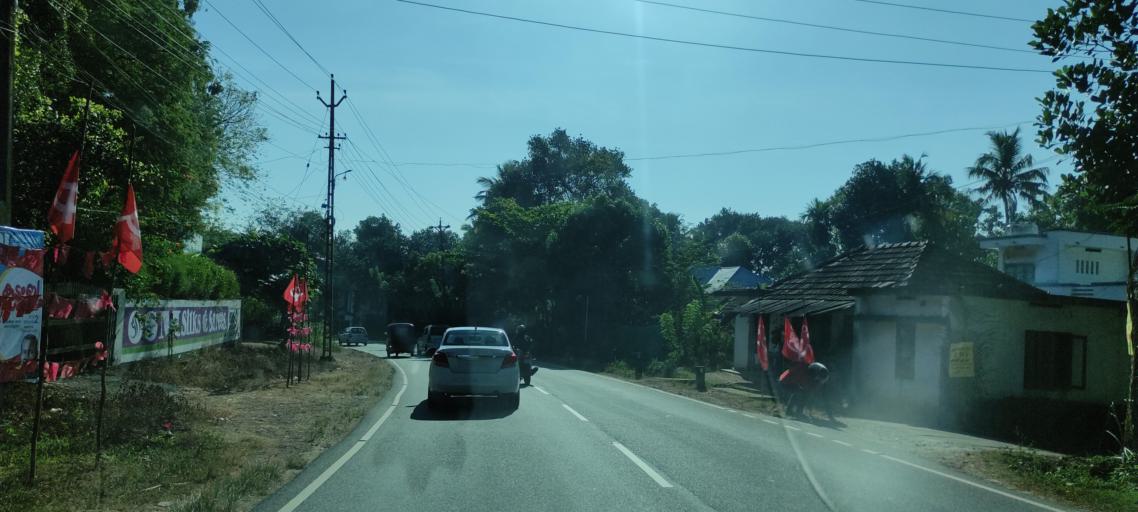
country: IN
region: Kerala
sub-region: Pattanamtitta
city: Adur
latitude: 9.1707
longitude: 76.6519
